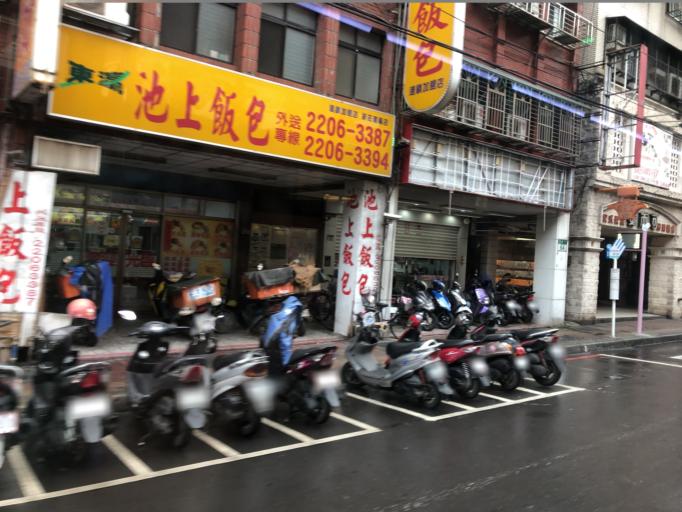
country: TW
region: Taipei
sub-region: Taipei
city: Banqiao
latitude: 25.0269
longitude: 121.4269
